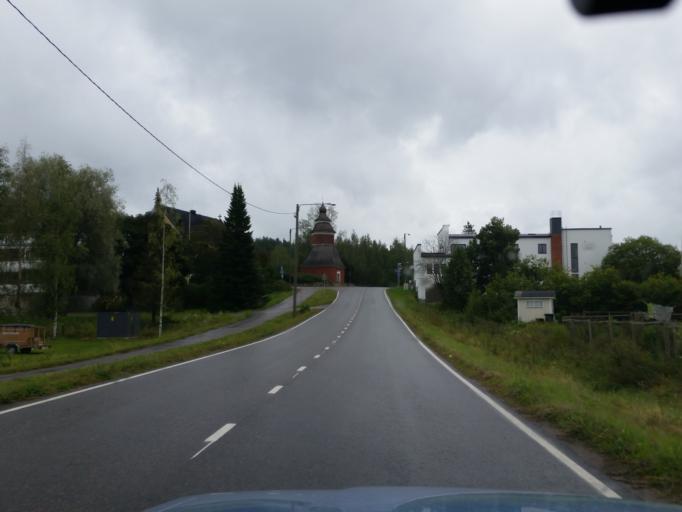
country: FI
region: Uusimaa
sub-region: Helsinki
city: Saukkola
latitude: 60.4727
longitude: 23.9804
